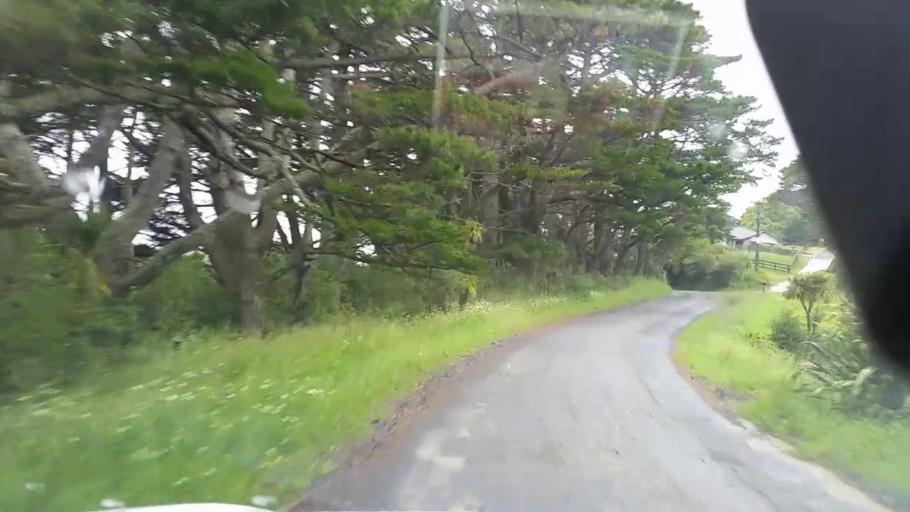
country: NZ
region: Auckland
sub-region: Auckland
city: Muriwai Beach
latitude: -36.8478
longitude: 174.5028
